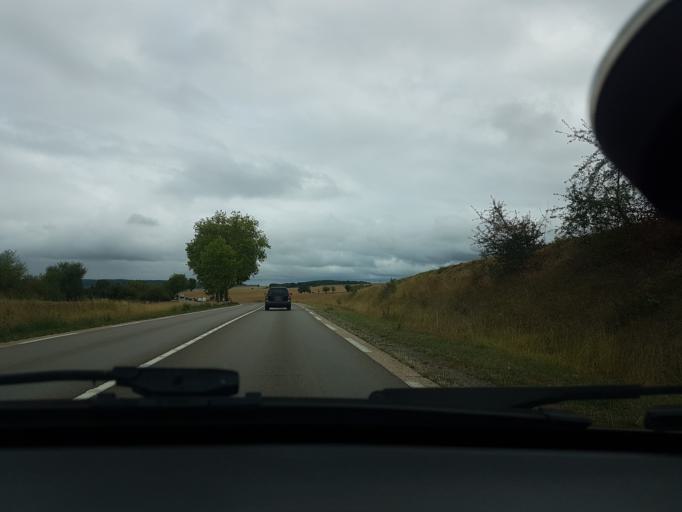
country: FR
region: Bourgogne
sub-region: Departement de l'Yonne
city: Saint-Bris-le-Vineux
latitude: 47.6965
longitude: 3.6354
